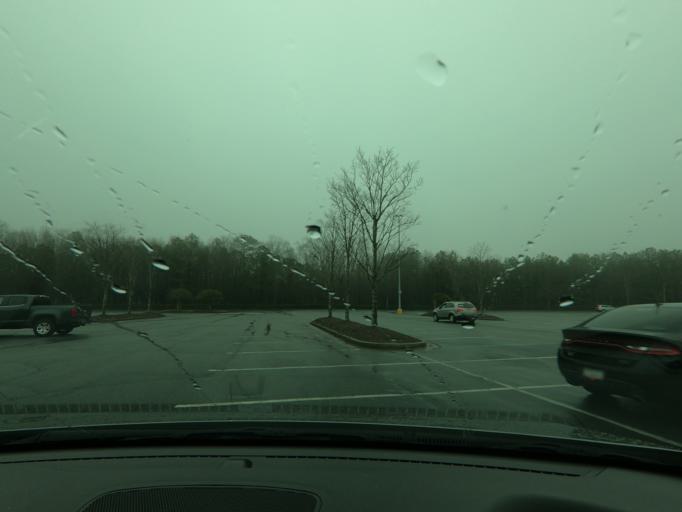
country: US
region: Georgia
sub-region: Fulton County
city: Alpharetta
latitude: 34.0488
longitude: -84.2915
